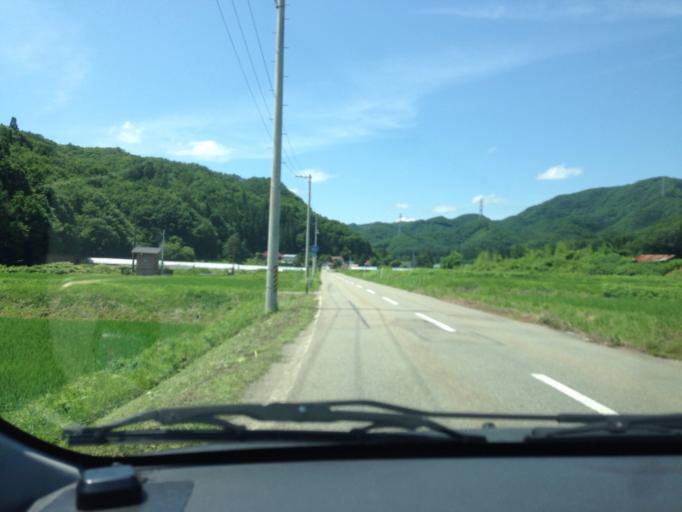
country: JP
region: Tochigi
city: Kuroiso
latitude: 37.2100
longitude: 139.7574
